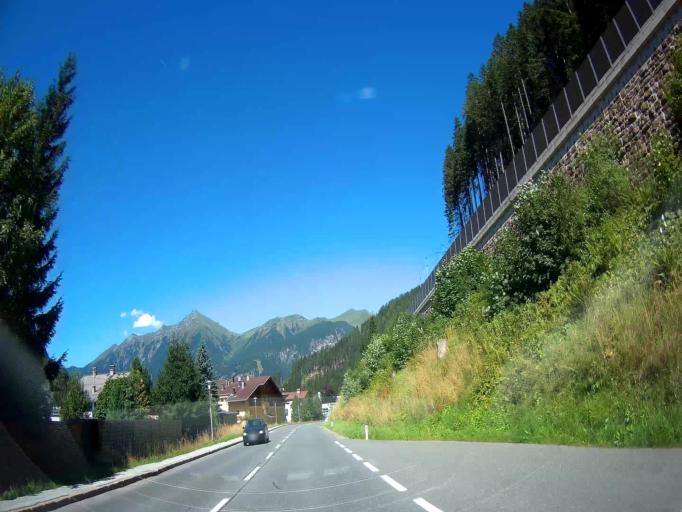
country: AT
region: Salzburg
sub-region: Politischer Bezirk Sankt Johann im Pongau
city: Bad Gastein
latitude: 47.1033
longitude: 13.1311
